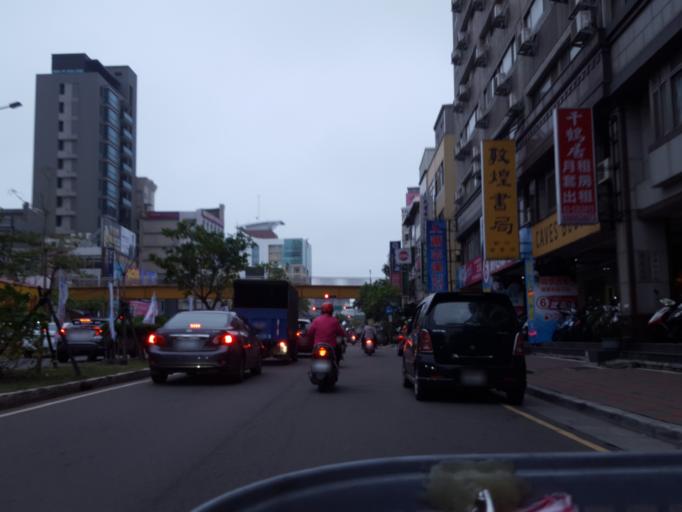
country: TW
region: Taiwan
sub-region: Hsinchu
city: Hsinchu
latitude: 24.8153
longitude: 120.9661
